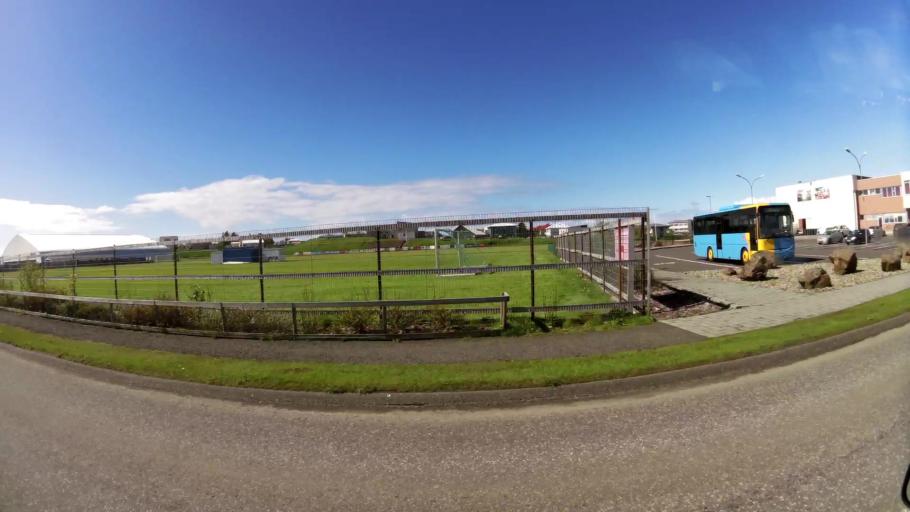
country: IS
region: East
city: Hoefn
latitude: 64.2537
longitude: -15.2056
